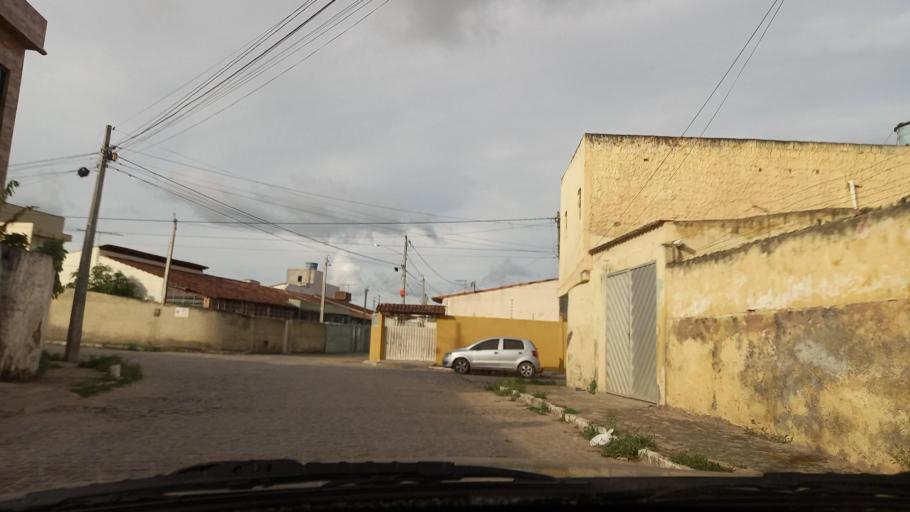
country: BR
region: Pernambuco
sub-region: Gravata
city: Gravata
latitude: -8.1998
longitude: -35.5604
